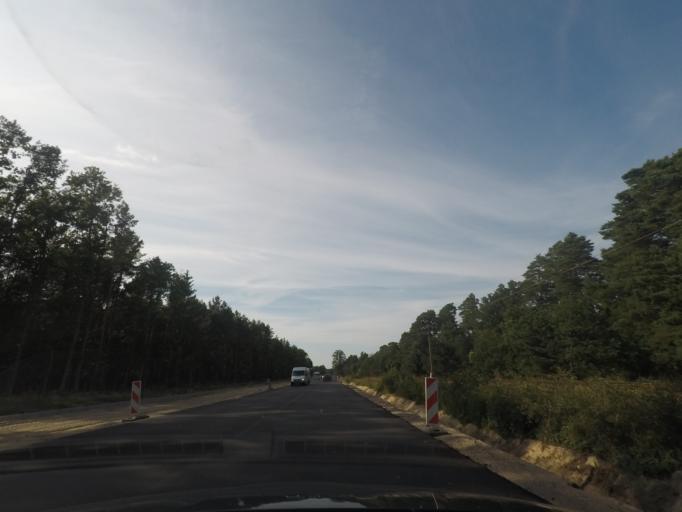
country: PL
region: Pomeranian Voivodeship
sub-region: Powiat leborski
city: Leba
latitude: 54.7204
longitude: 17.5732
